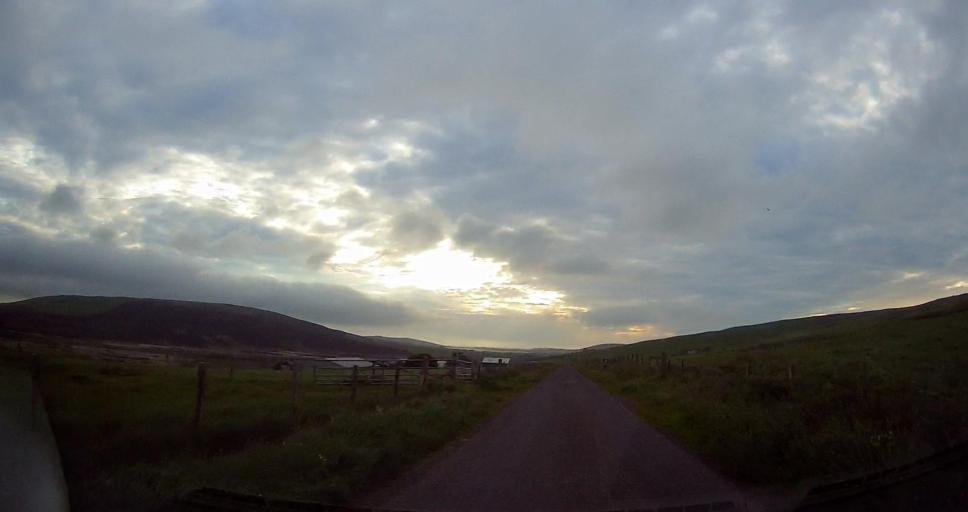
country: GB
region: Scotland
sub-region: Orkney Islands
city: Stromness
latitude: 59.0963
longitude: -3.1916
